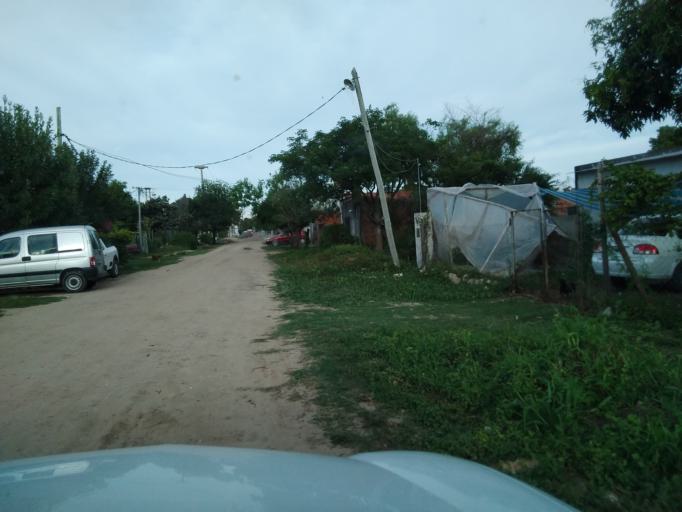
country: AR
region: Corrientes
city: Corrientes
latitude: -27.4913
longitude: -58.8481
